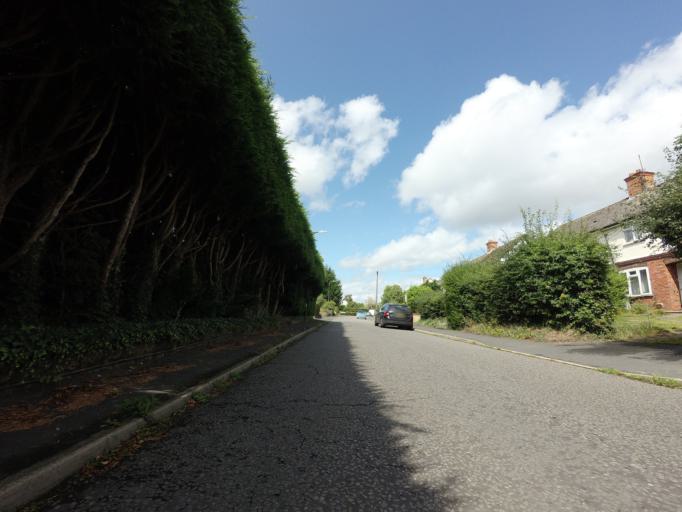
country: GB
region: England
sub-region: Kent
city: Hadlow
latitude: 51.2246
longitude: 0.3341
